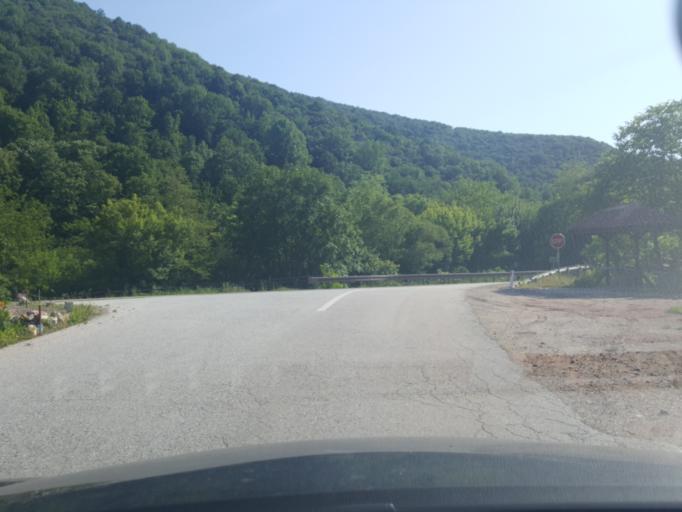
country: RS
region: Central Serbia
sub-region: Nisavski Okrug
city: Razanj
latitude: 43.8599
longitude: 21.6245
